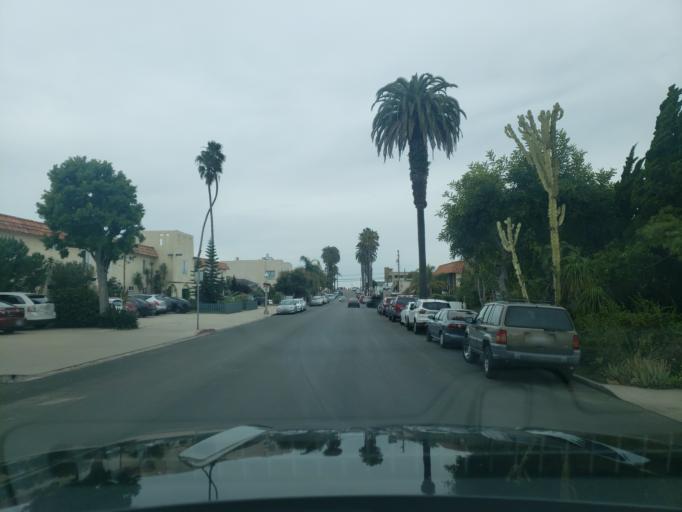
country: US
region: California
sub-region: San Diego County
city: Coronado
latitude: 32.7453
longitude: -117.2506
